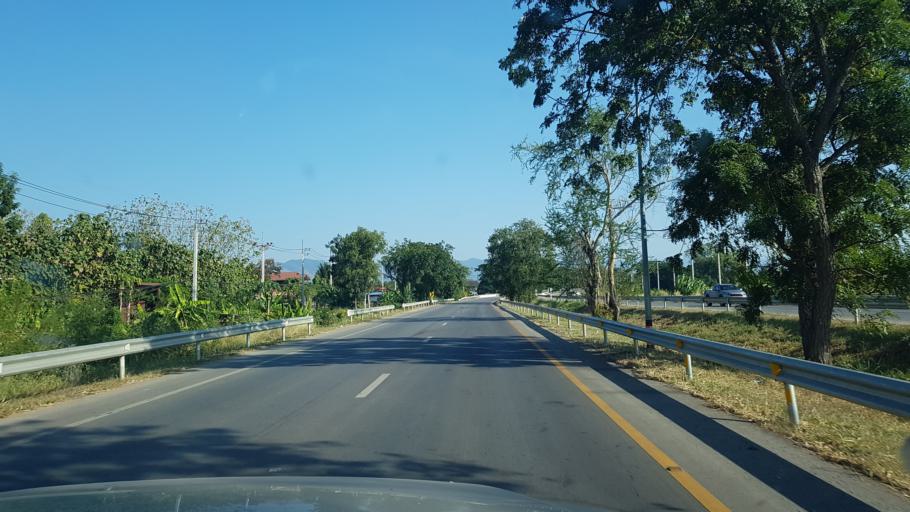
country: TH
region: Phetchabun
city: Lom Sak
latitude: 16.7367
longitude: 101.2319
